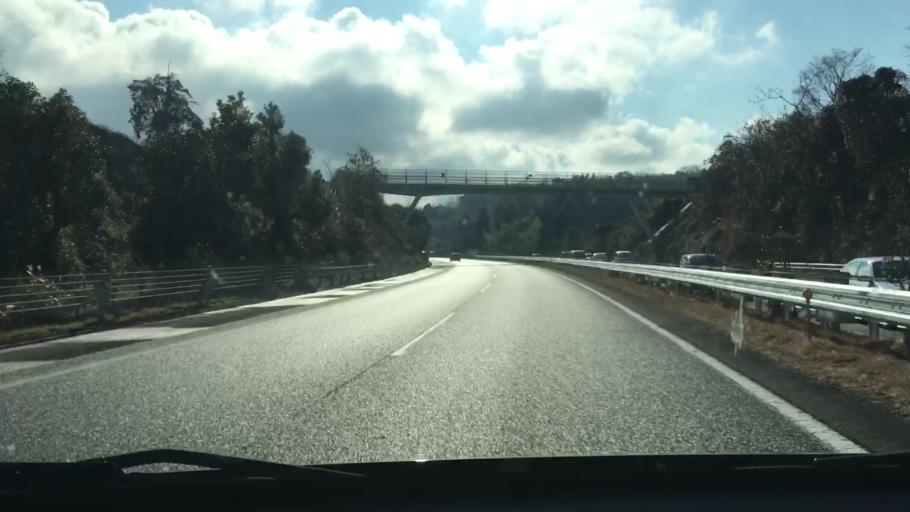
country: JP
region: Kumamoto
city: Matsubase
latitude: 32.5610
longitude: 130.6978
